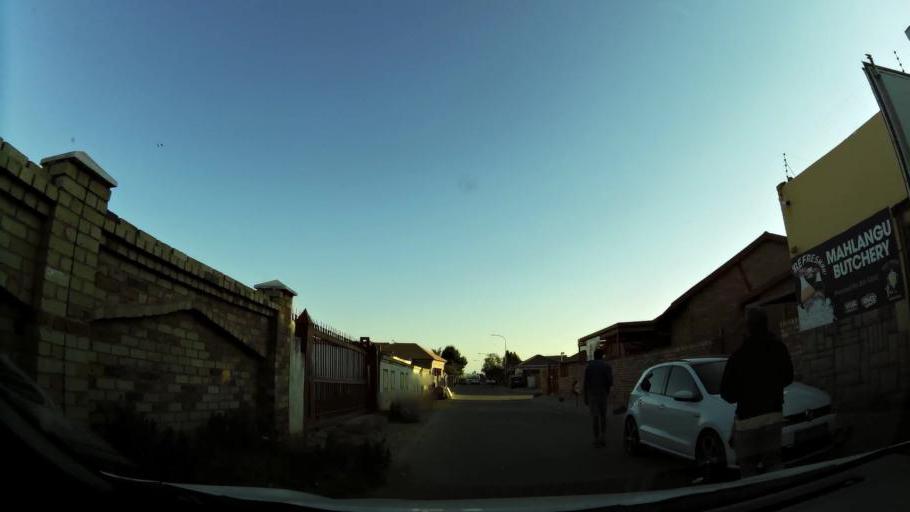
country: ZA
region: Gauteng
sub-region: City of Tshwane Metropolitan Municipality
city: Cullinan
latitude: -25.7257
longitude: 28.3942
